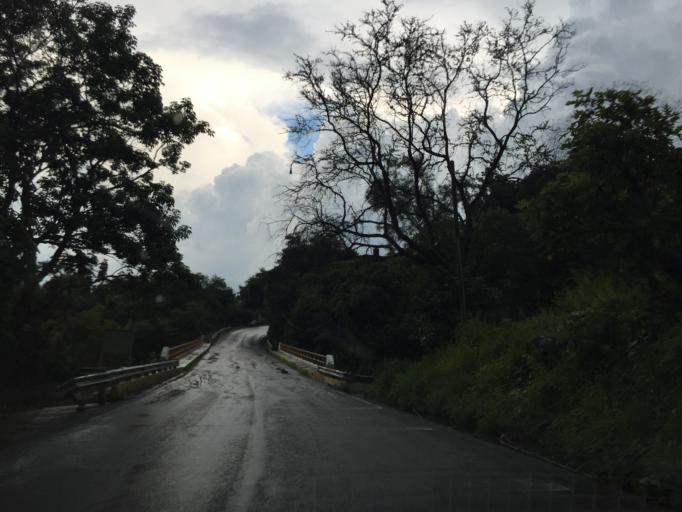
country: MX
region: Colima
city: Queseria
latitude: 19.3901
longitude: -103.5673
